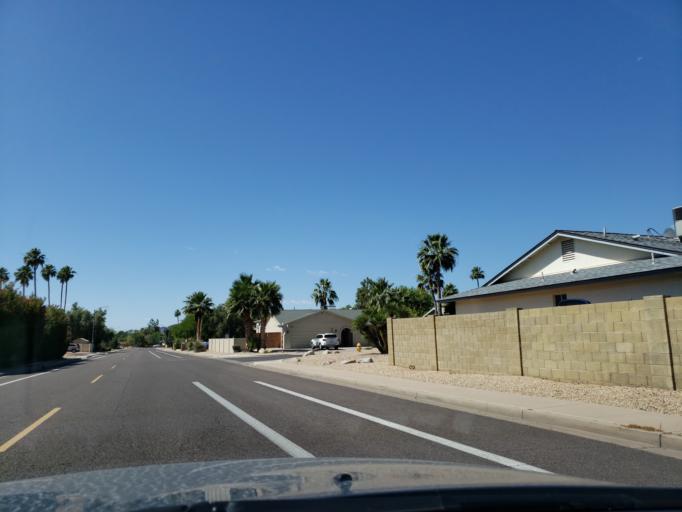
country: US
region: Arizona
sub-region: Maricopa County
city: Paradise Valley
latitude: 33.6140
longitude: -111.9518
